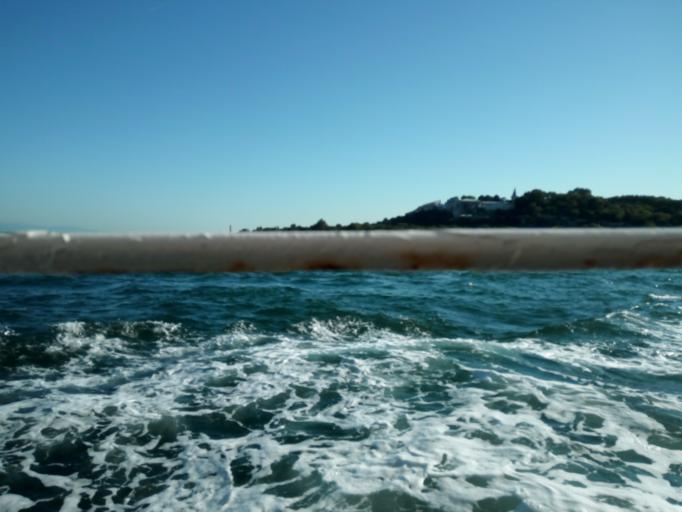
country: TR
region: Istanbul
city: Eminoenue
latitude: 41.0173
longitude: 28.9912
